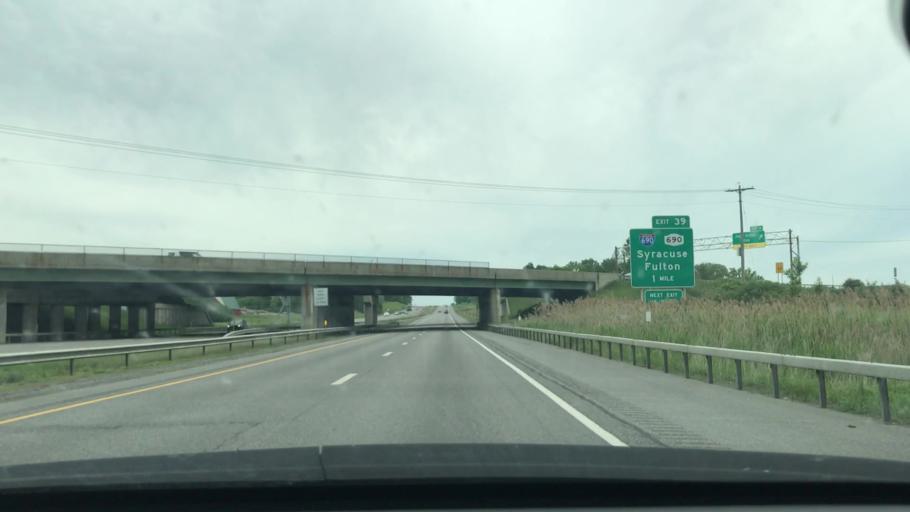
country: US
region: New York
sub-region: Onondaga County
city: Seneca Knolls
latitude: 43.1118
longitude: -76.2636
